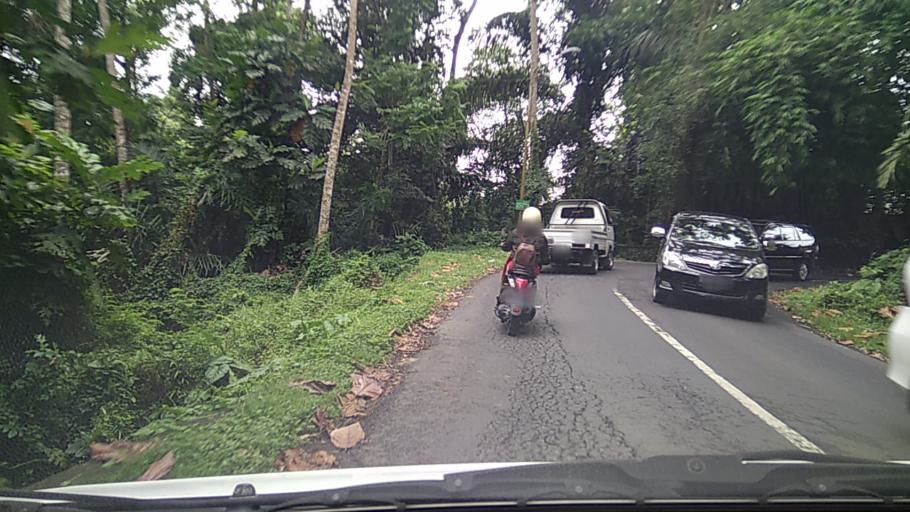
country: ID
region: Bali
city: Banjar Tebongkang
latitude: -8.5228
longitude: 115.2348
